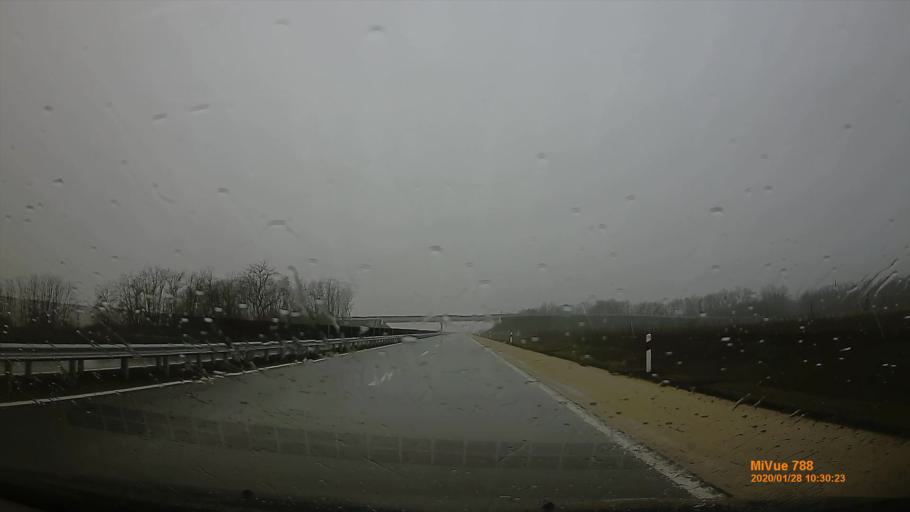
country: HU
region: Pest
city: Gomba
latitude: 47.3314
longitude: 19.5190
